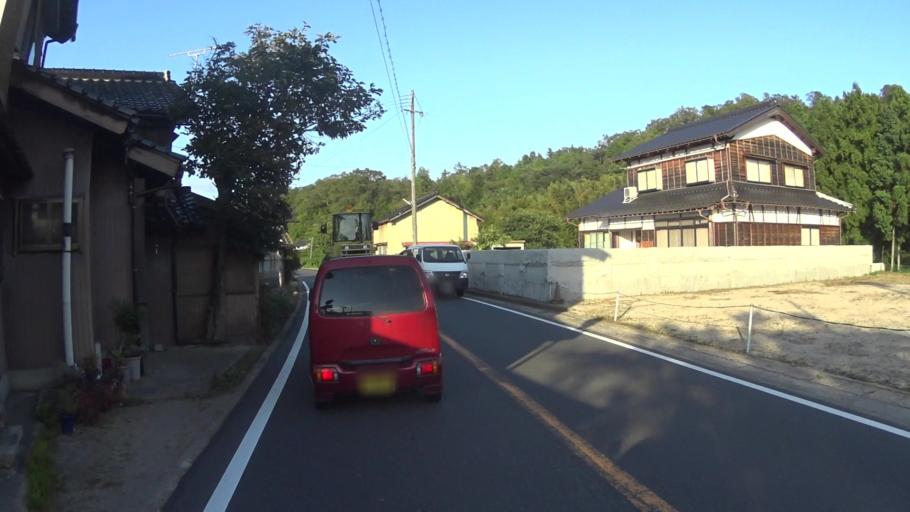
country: JP
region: Kyoto
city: Miyazu
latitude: 35.5937
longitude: 135.0426
